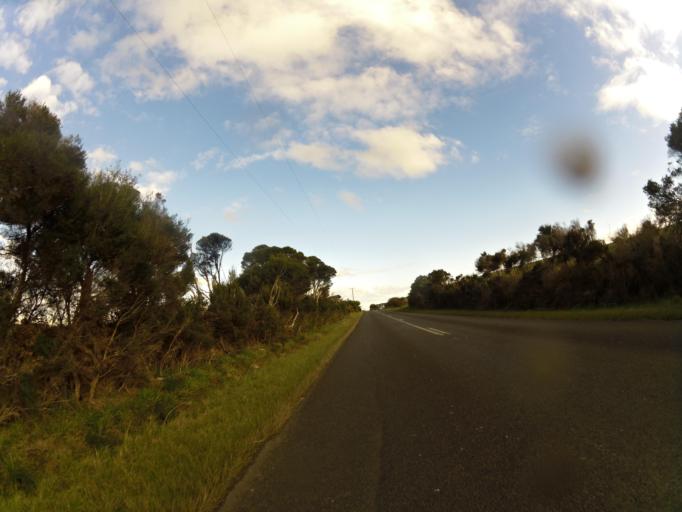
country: AU
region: Victoria
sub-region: Bass Coast
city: North Wonthaggi
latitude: -38.5513
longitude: 145.5499
